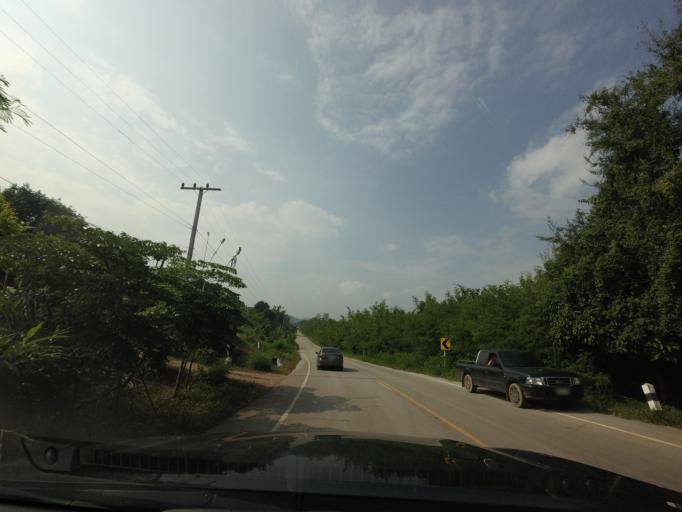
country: TH
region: Loei
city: Chiang Khan
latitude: 17.8627
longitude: 101.5735
